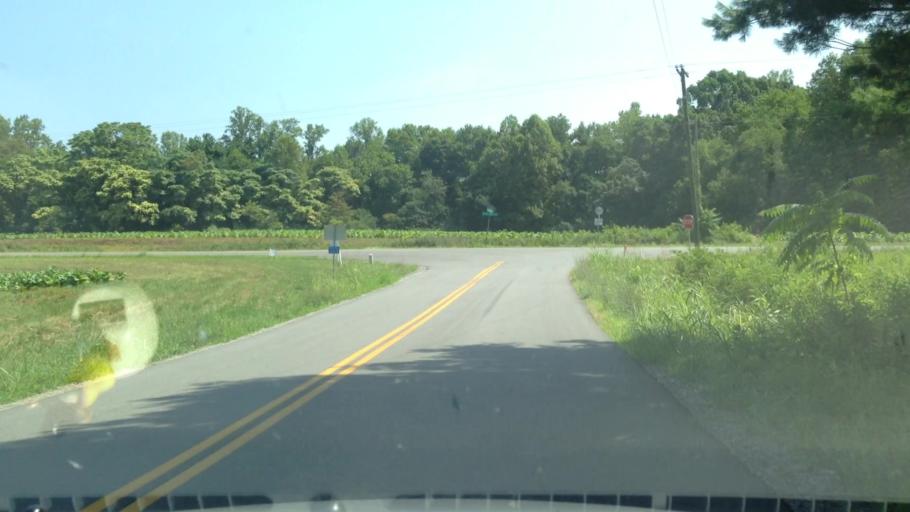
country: US
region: Virginia
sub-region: Patrick County
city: Patrick Springs
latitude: 36.6035
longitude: -80.1696
